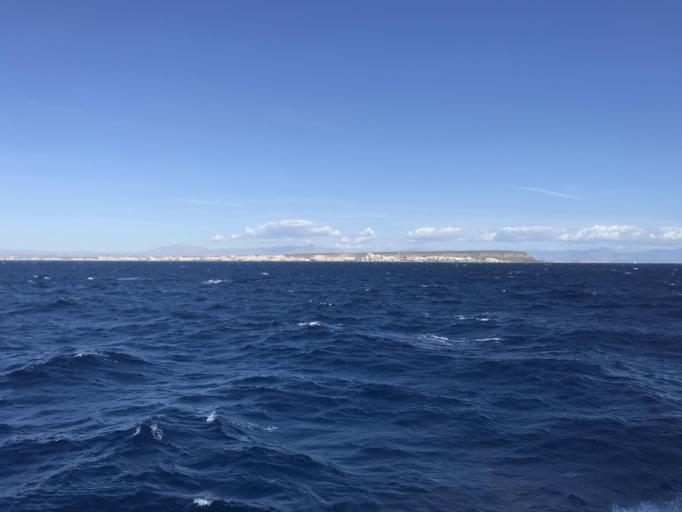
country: ES
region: Valencia
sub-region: Provincia de Alicante
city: Santa Pola
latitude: 38.1418
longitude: -0.5240
